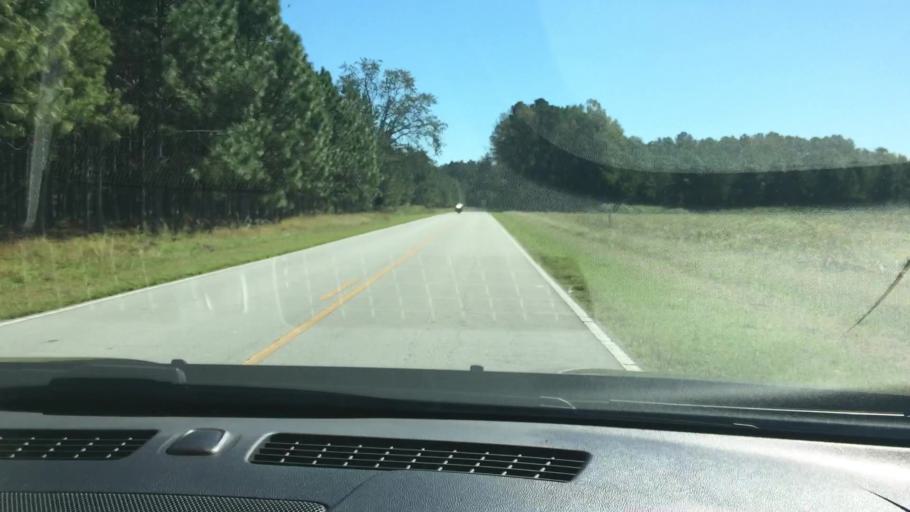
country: US
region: North Carolina
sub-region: Pitt County
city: Grifton
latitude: 35.3356
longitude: -77.3050
